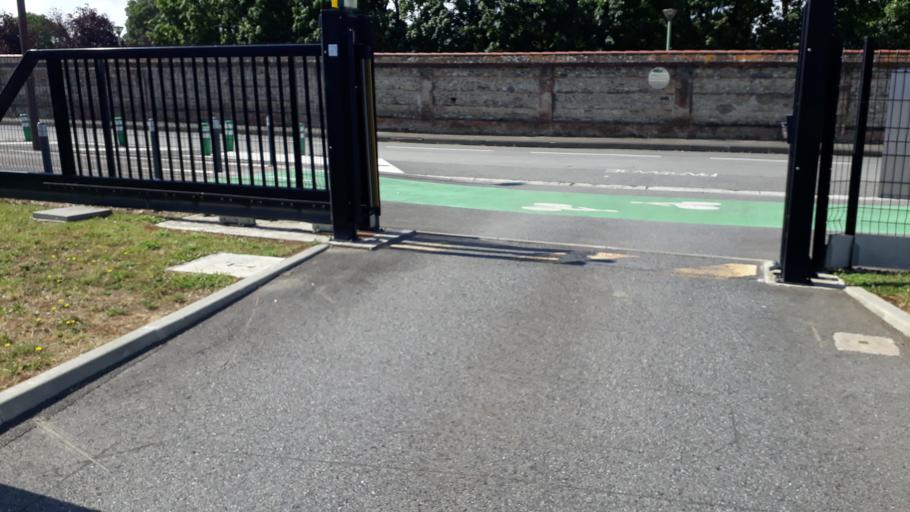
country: FR
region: Midi-Pyrenees
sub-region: Departement de la Haute-Garonne
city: Portet-sur-Garonne
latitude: 43.5634
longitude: 1.4230
